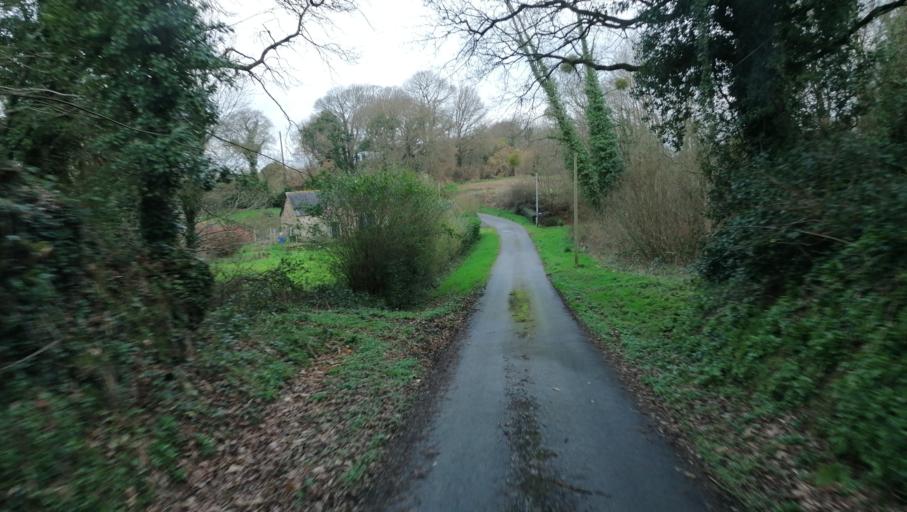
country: FR
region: Brittany
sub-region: Departement des Cotes-d'Armor
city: Pommerit-le-Vicomte
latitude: 48.6482
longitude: -3.0784
